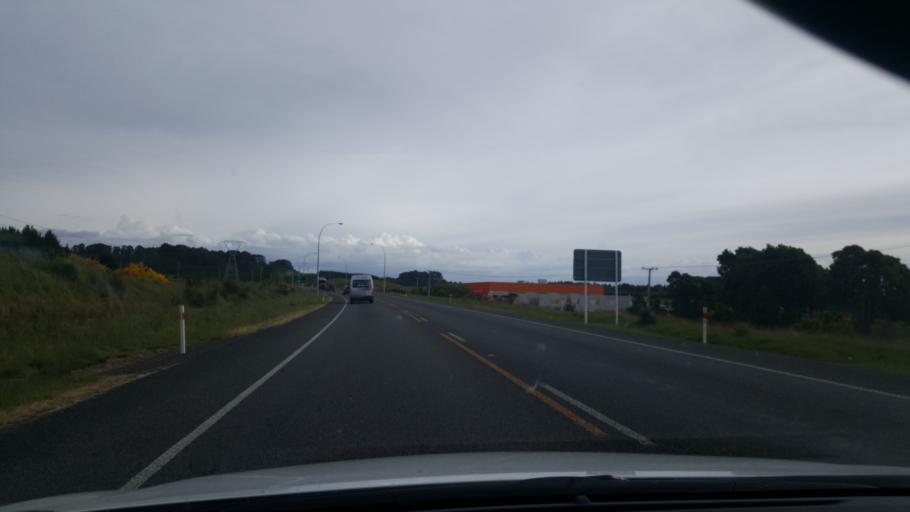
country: NZ
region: Waikato
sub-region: Taupo District
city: Taupo
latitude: -38.7002
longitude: 176.1119
